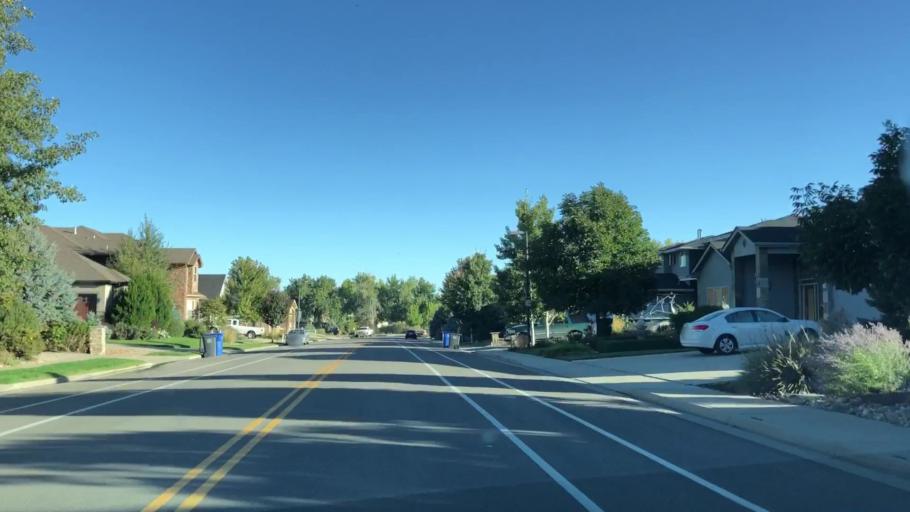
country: US
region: Colorado
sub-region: Larimer County
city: Loveland
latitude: 40.4548
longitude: -105.0320
